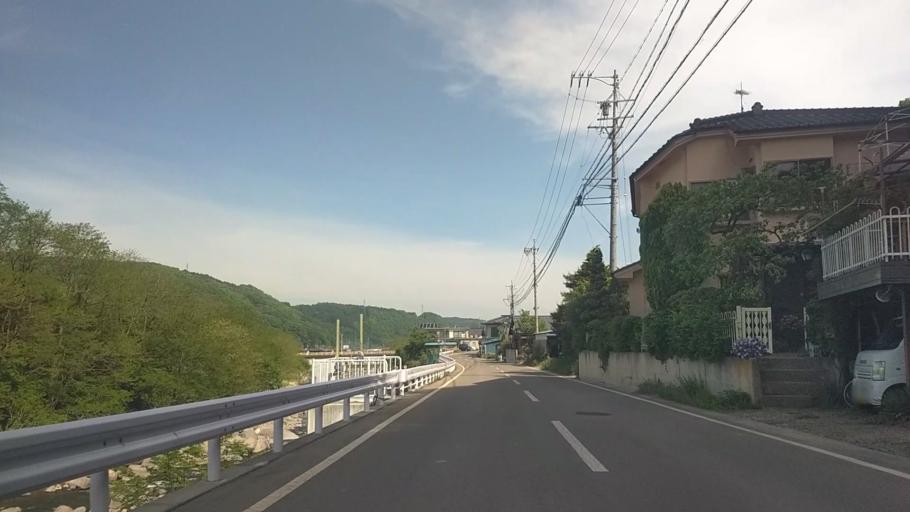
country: JP
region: Nagano
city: Saku
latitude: 36.1107
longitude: 138.4794
